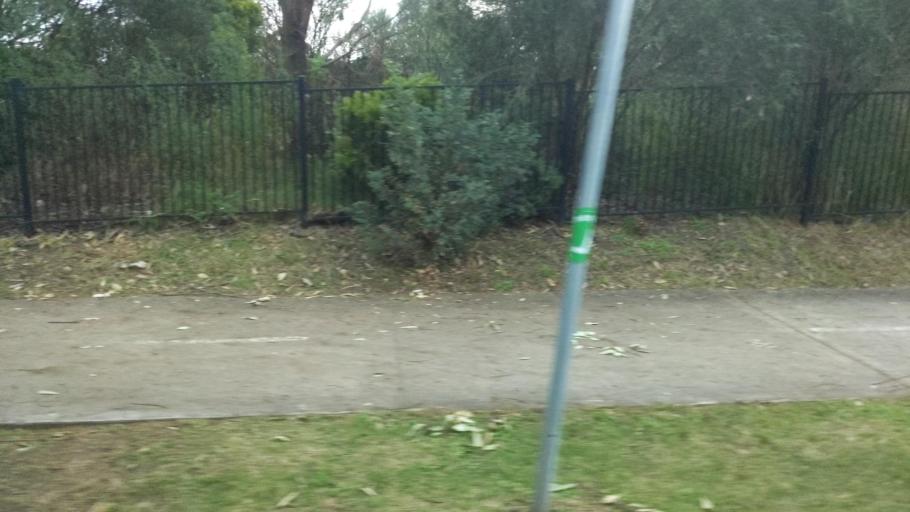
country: AU
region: New South Wales
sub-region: Blacktown
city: Glendenning
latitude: -33.7232
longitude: 150.8595
